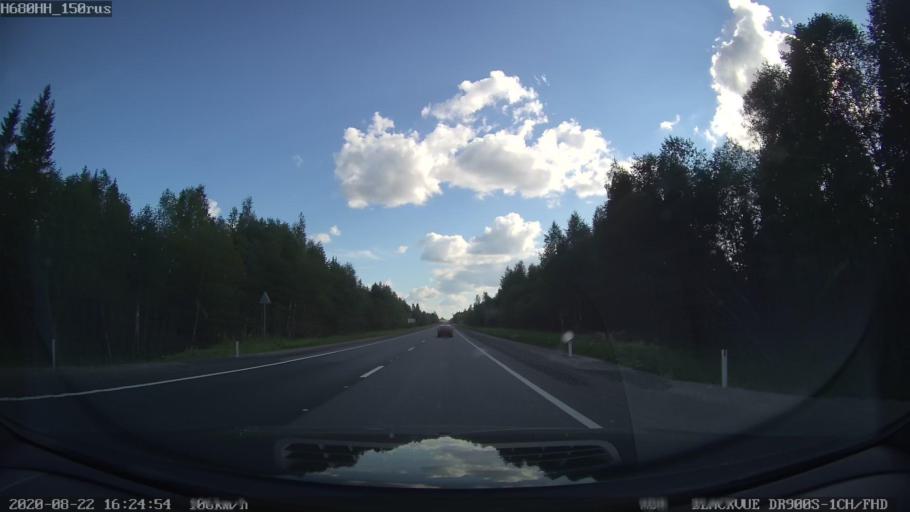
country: RU
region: Tverskaya
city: Rameshki
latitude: 57.3296
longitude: 36.0928
